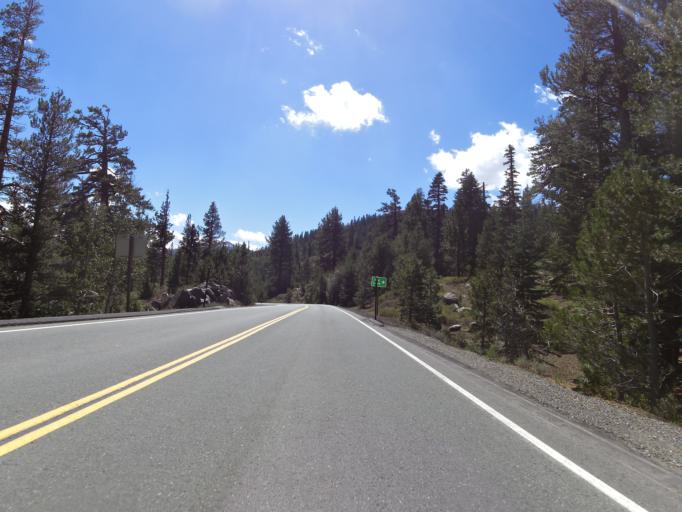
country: US
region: California
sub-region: El Dorado County
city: South Lake Tahoe
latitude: 38.7011
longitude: -119.9667
